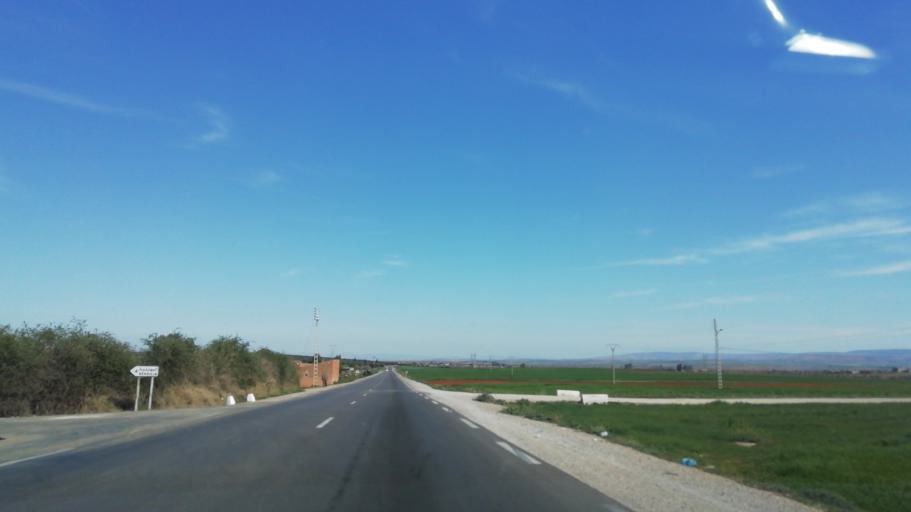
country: DZ
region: Mascara
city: Mascara
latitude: 35.4179
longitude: 0.4124
